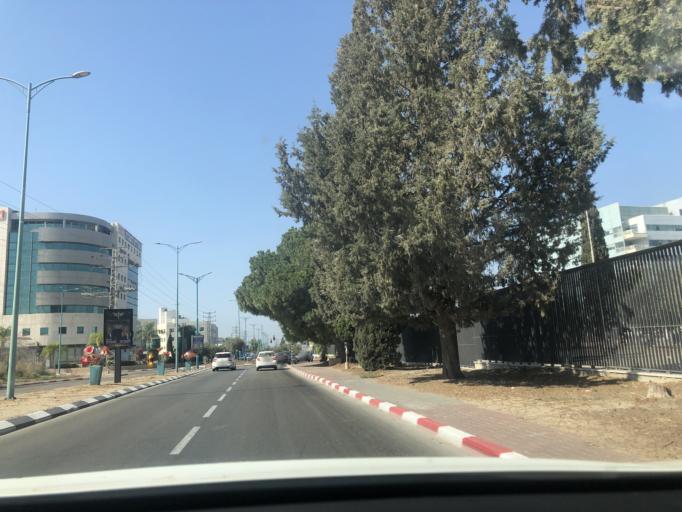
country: IL
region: Central District
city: Lod
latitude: 31.9625
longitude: 34.8995
